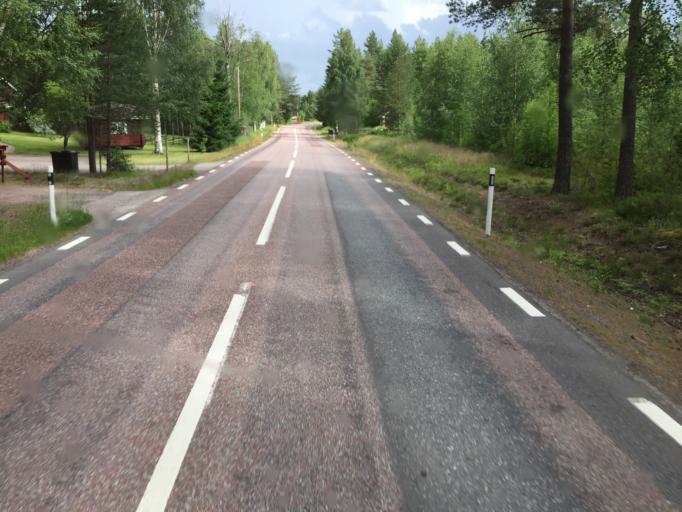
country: SE
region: Dalarna
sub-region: Vansbro Kommun
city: Jarna
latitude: 60.5272
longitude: 14.4427
